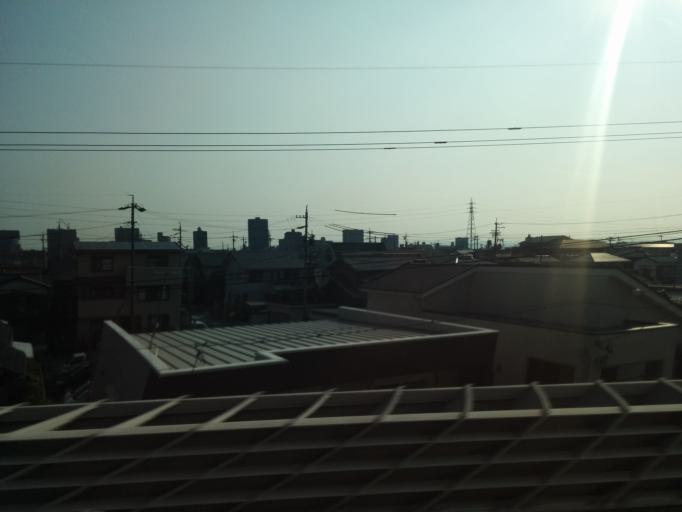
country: JP
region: Aichi
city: Anjo
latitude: 34.9495
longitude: 137.0785
